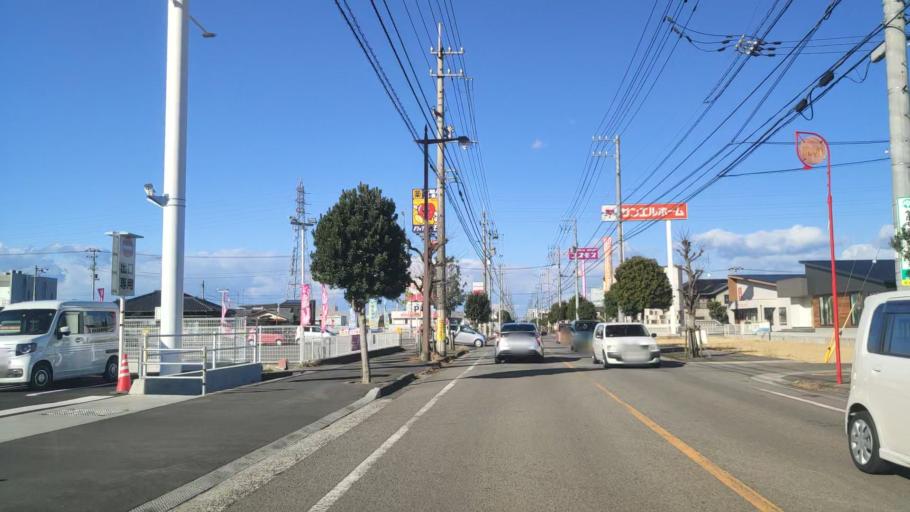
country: JP
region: Ehime
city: Saijo
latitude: 33.9245
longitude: 133.1911
